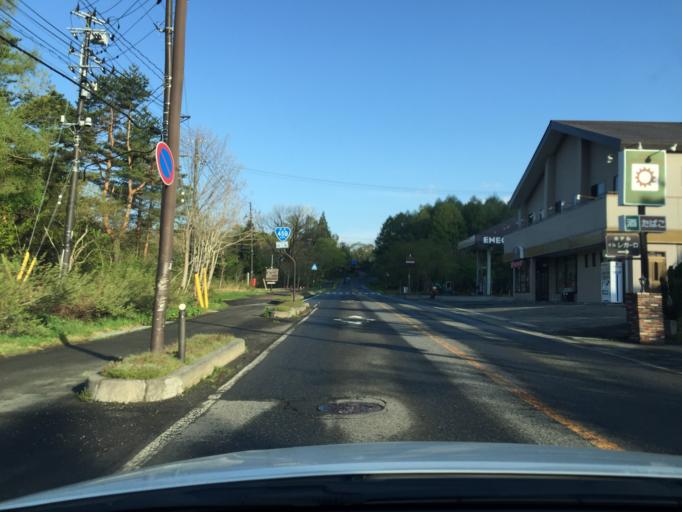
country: JP
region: Fukushima
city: Inawashiro
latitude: 37.6573
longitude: 140.0890
